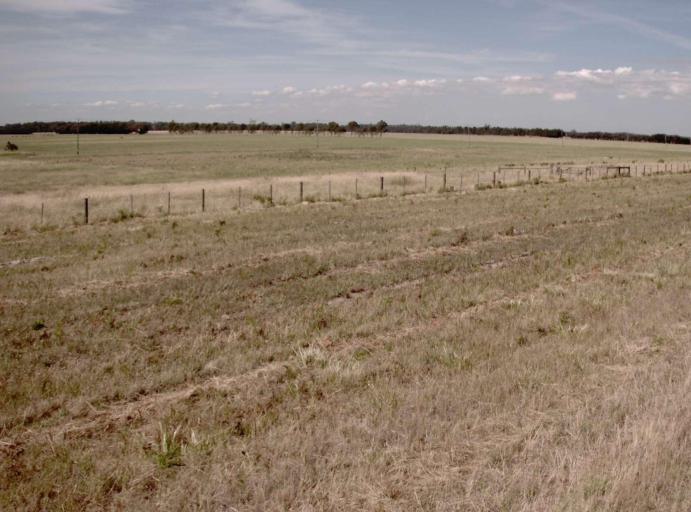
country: AU
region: Victoria
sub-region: Wellington
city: Heyfield
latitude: -38.1619
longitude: 146.8724
